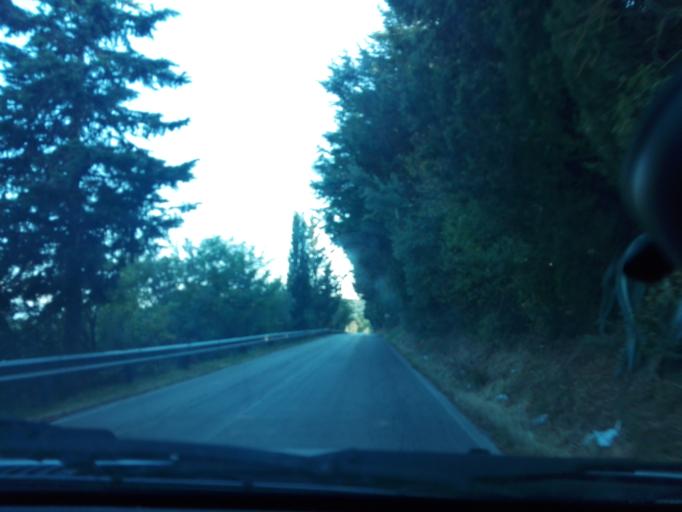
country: IT
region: Abruzzo
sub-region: Provincia di Pescara
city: Cappelle sul Tavo
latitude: 42.4542
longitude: 14.0917
